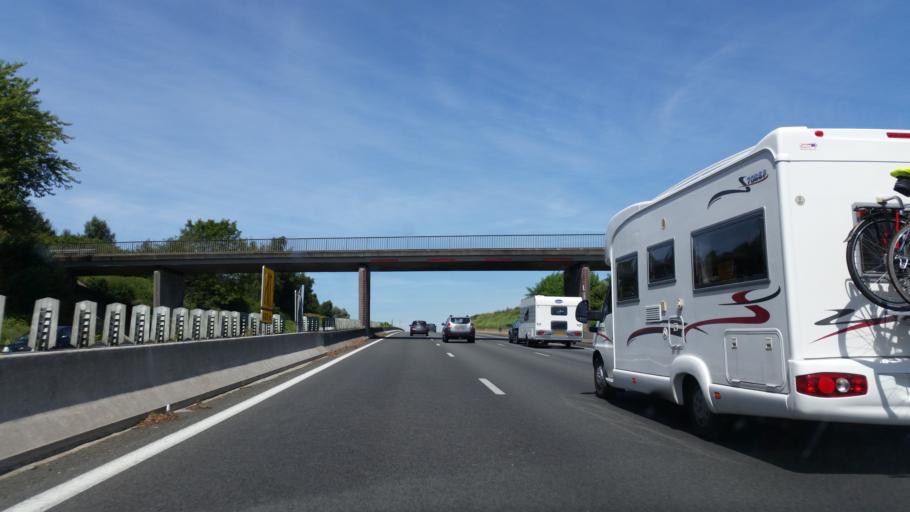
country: FR
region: Nord-Pas-de-Calais
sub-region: Departement du Pas-de-Calais
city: Croisilles
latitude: 50.1977
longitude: 2.8692
